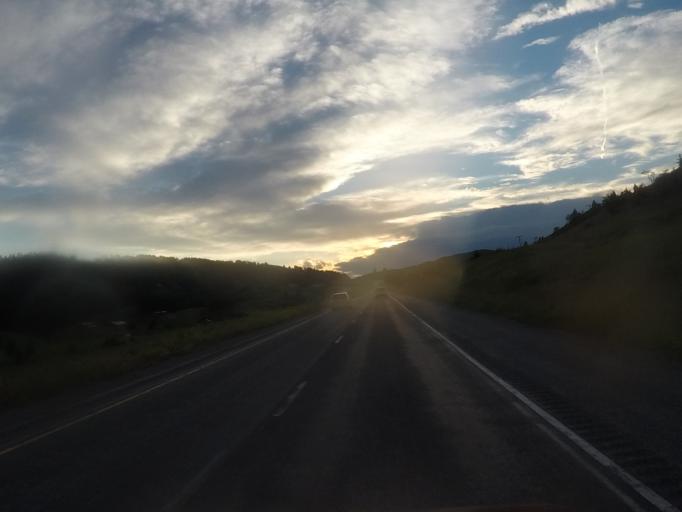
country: US
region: Montana
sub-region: Park County
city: Livingston
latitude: 45.6592
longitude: -110.7838
